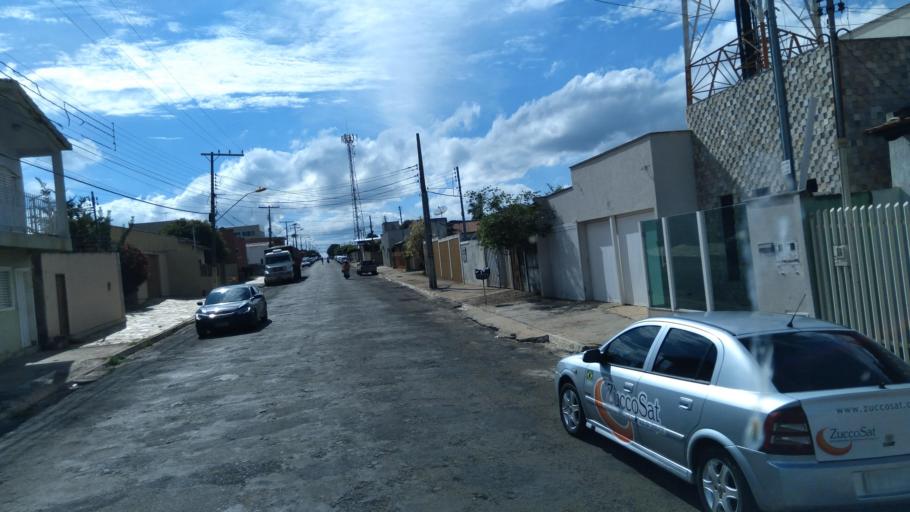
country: BR
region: Goias
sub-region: Mineiros
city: Mineiros
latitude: -17.5610
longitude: -52.5572
